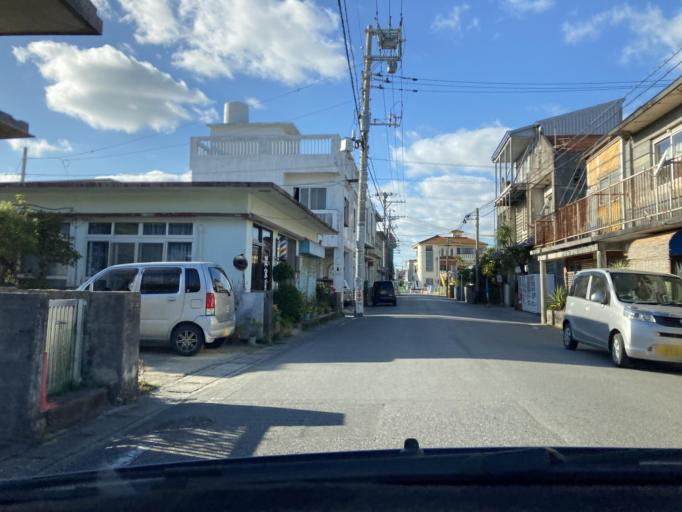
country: JP
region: Okinawa
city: Katsuren-haebaru
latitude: 26.3224
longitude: 127.9097
